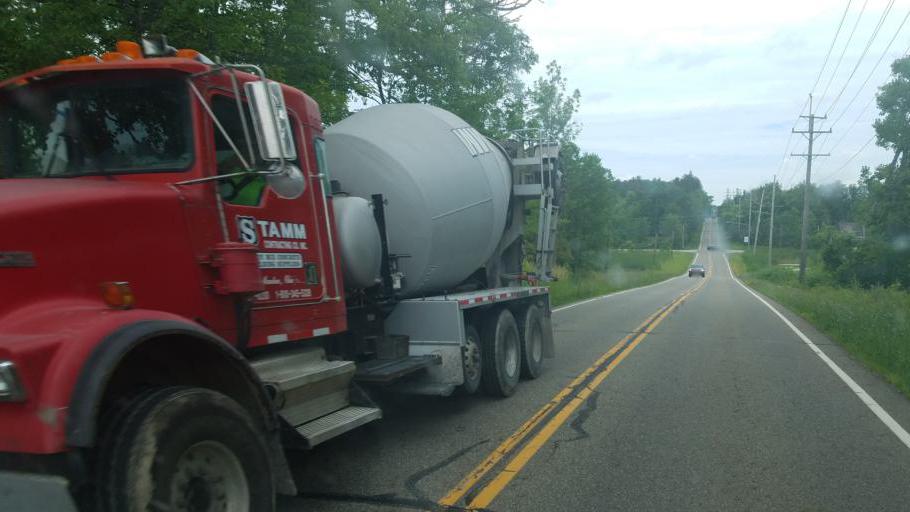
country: US
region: Ohio
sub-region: Geauga County
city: Burton
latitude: 41.4783
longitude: -81.2439
